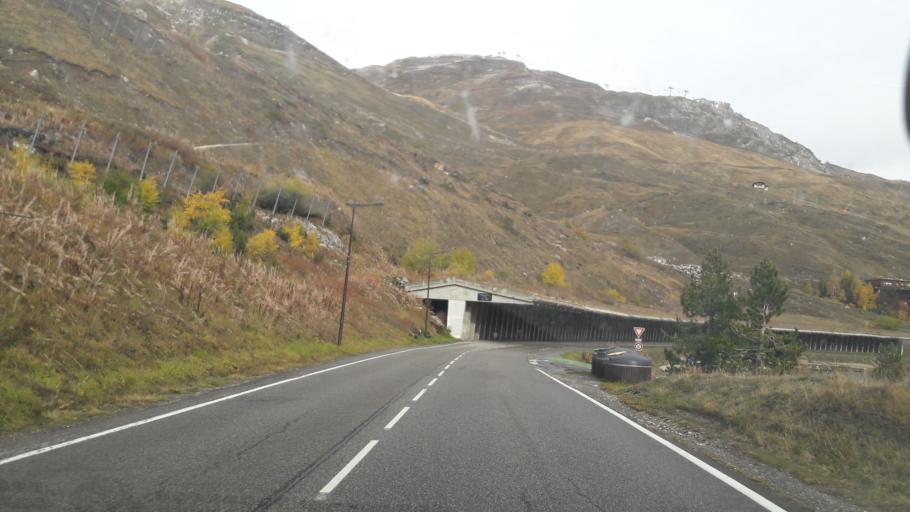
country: FR
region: Rhone-Alpes
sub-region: Departement de la Savoie
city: Tignes
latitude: 45.4639
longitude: 6.8988
